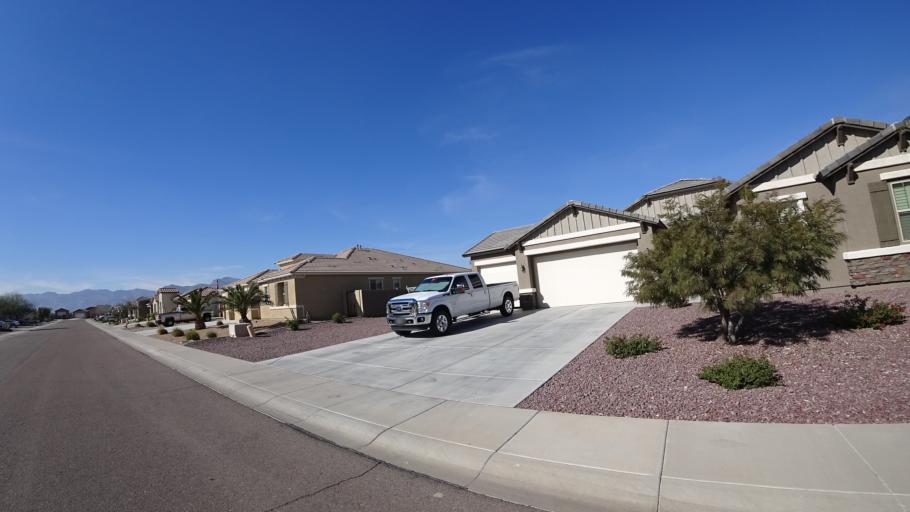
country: US
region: Arizona
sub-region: Maricopa County
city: Citrus Park
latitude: 33.5186
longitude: -112.4581
